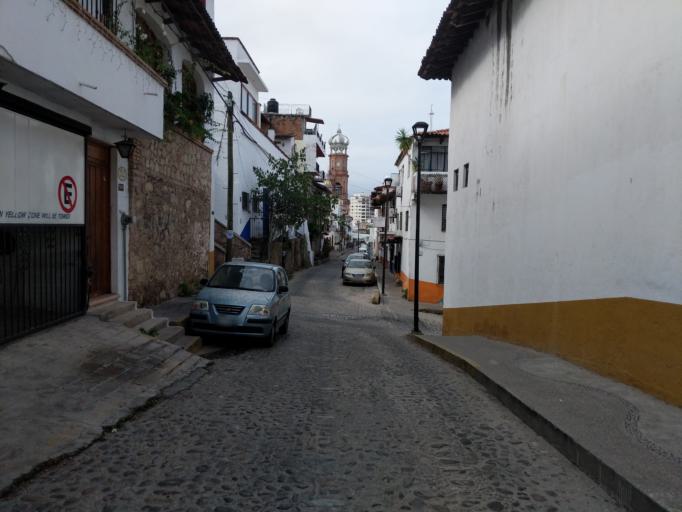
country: MX
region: Jalisco
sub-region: Puerto Vallarta
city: Puerto Vallarta
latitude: 20.6099
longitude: -105.2338
